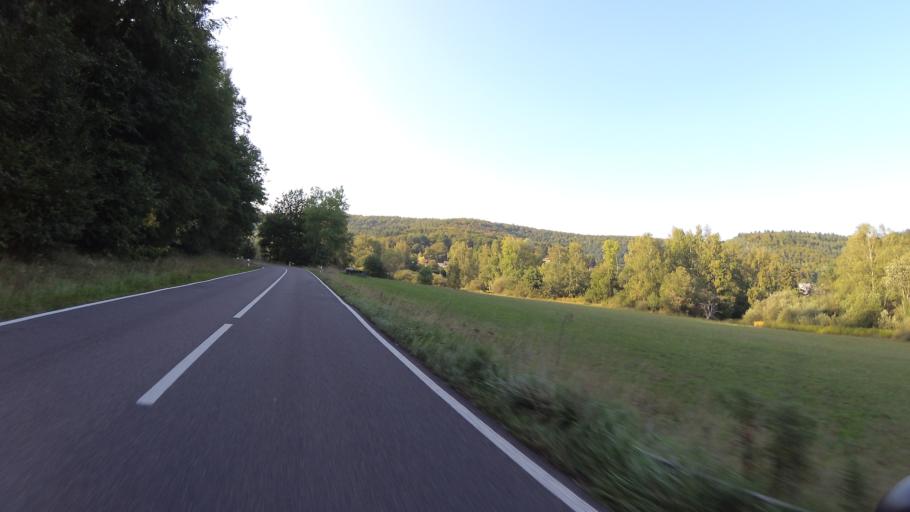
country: DE
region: Saarland
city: Sankt Ingbert
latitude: 49.2506
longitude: 7.1268
